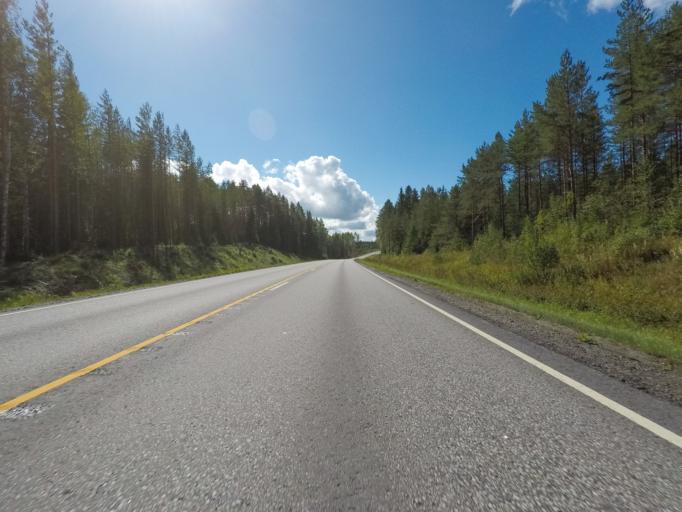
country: FI
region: Central Finland
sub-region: Jyvaeskylae
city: Hankasalmi
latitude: 62.3746
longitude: 26.5877
